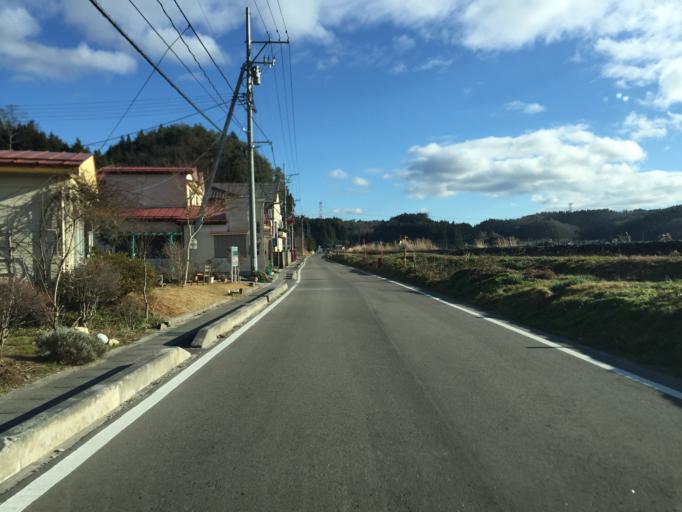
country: JP
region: Fukushima
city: Funehikimachi-funehiki
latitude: 37.2519
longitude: 140.6649
